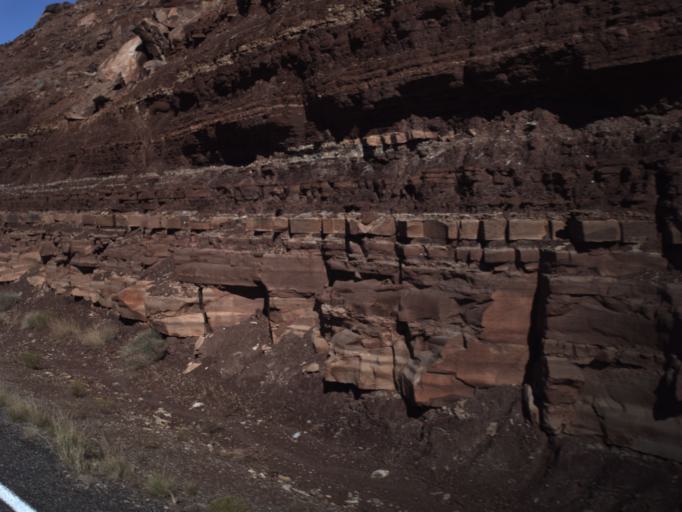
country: US
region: Utah
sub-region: San Juan County
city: Blanding
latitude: 37.8819
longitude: -110.4216
